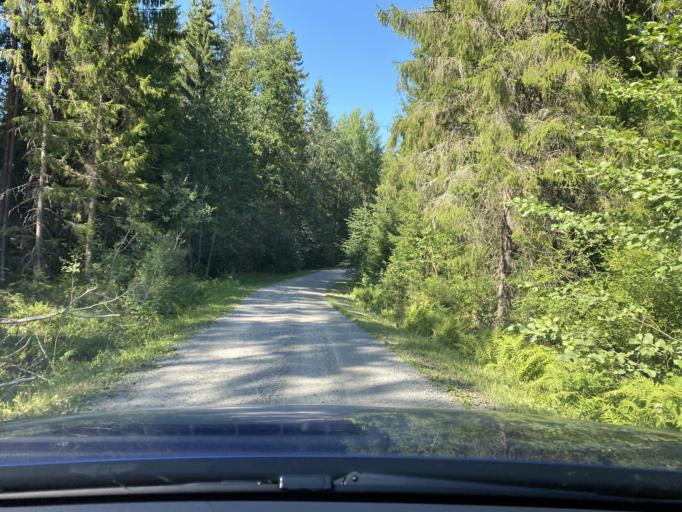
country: FI
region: Satakunta
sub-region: Rauma
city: Kiukainen
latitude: 61.1391
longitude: 22.0251
